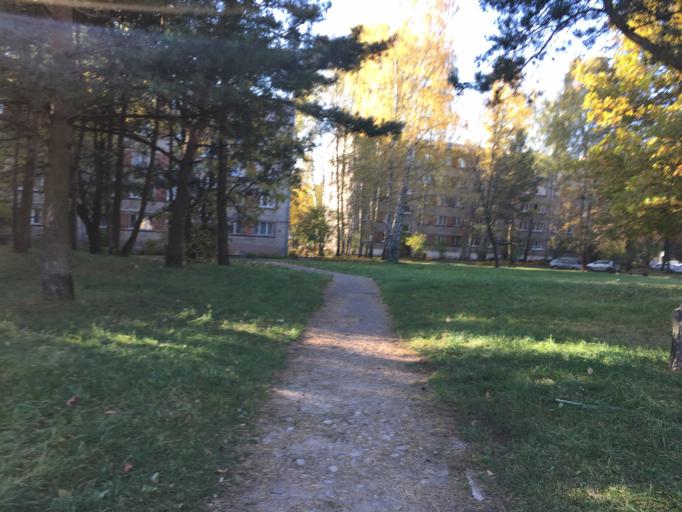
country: LV
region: Marupe
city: Marupe
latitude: 56.9436
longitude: 24.0605
